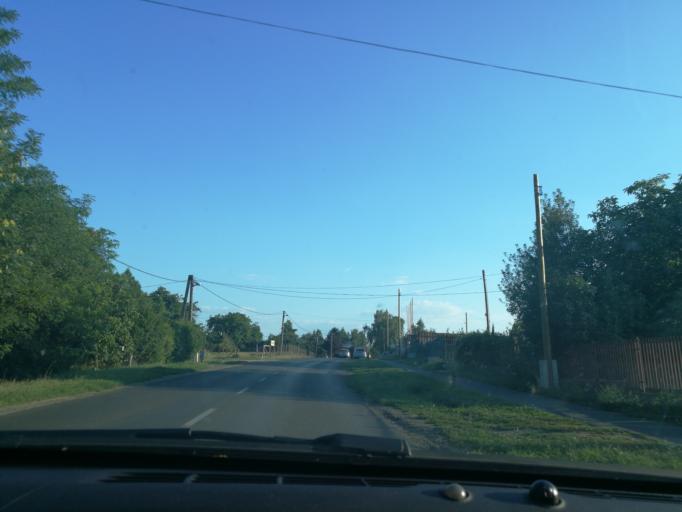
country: HU
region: Szabolcs-Szatmar-Bereg
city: Kotaj
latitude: 48.0240
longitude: 21.7448
